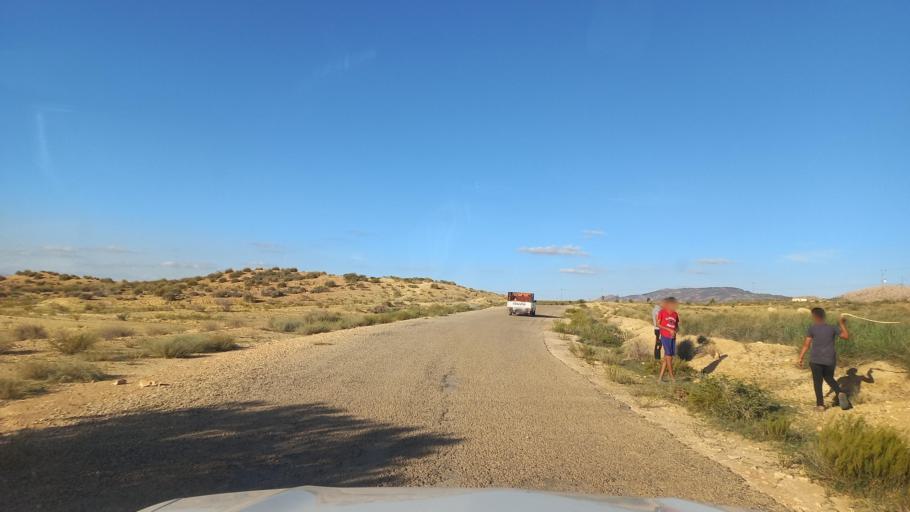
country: TN
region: Al Qasrayn
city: Sbiba
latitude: 35.3529
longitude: 9.1355
